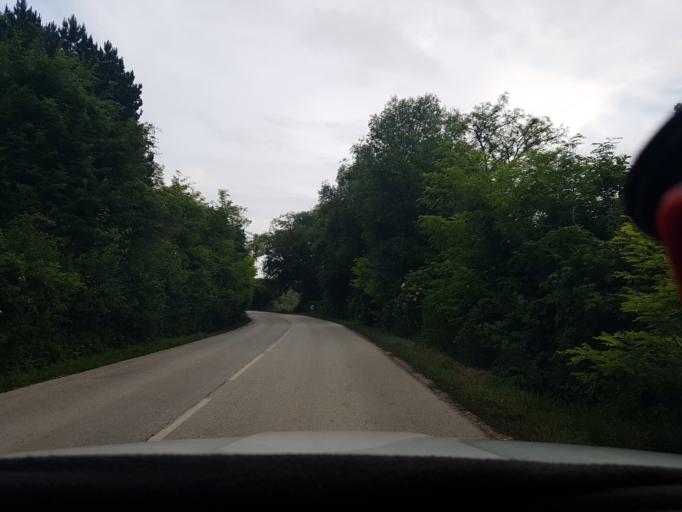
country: HU
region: Pest
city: Perbal
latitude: 47.6280
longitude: 18.7603
